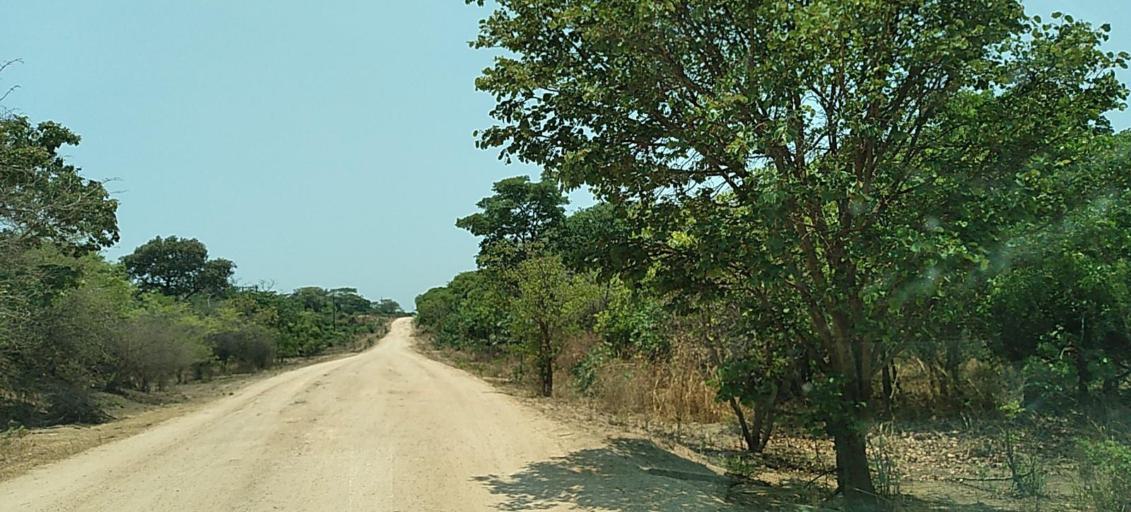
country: ZM
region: Copperbelt
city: Mpongwe
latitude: -13.8143
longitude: 27.8482
